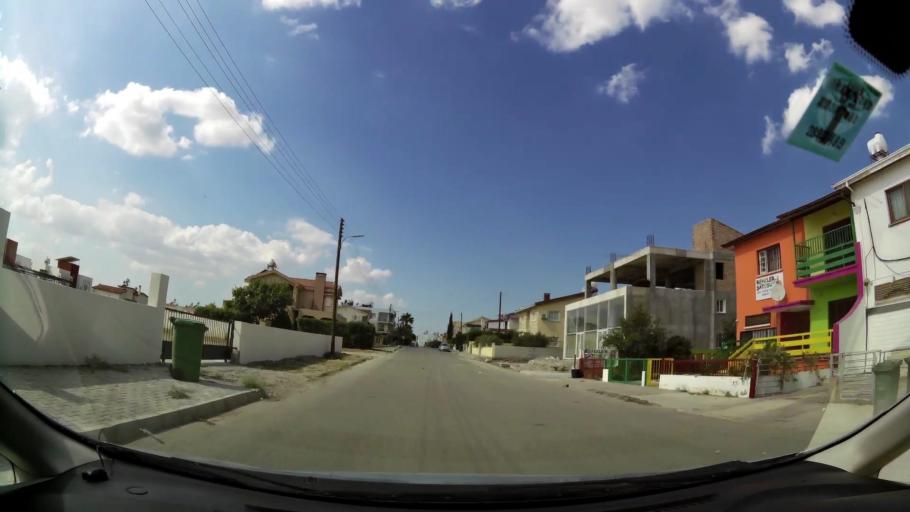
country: CY
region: Lefkosia
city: Nicosia
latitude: 35.2229
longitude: 33.2975
